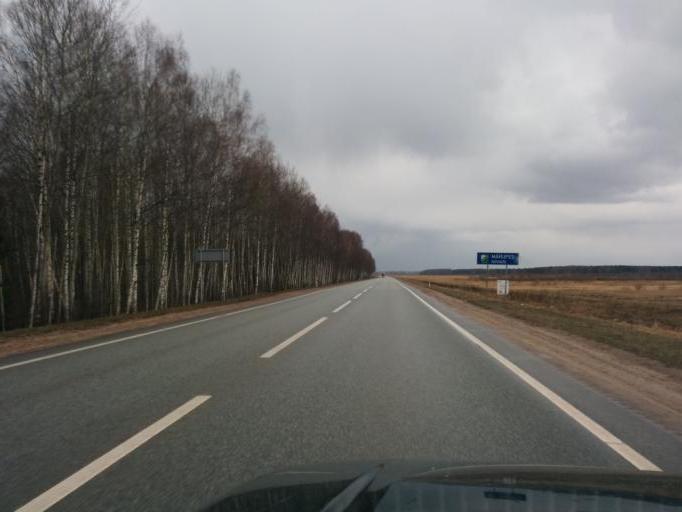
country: LV
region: Marupe
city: Marupe
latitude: 56.8494
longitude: 24.0094
